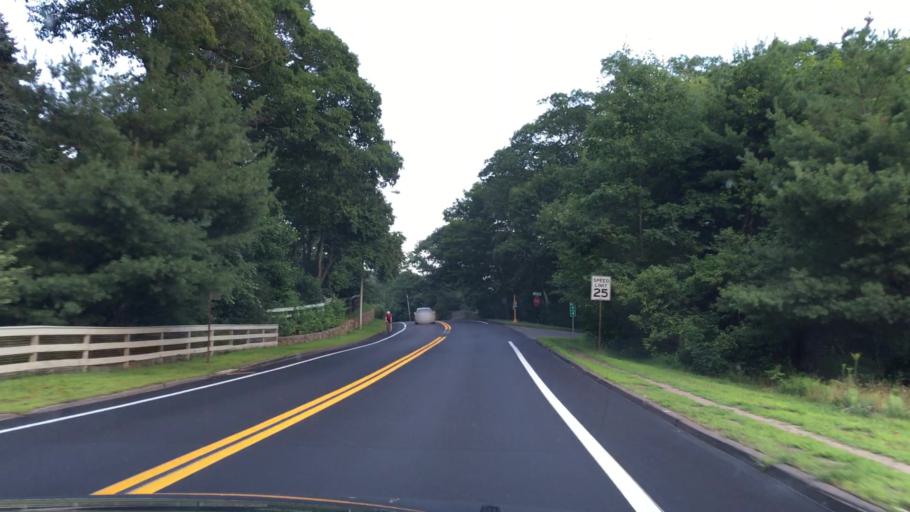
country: US
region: Massachusetts
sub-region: Essex County
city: Essex
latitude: 42.5805
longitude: -70.7318
